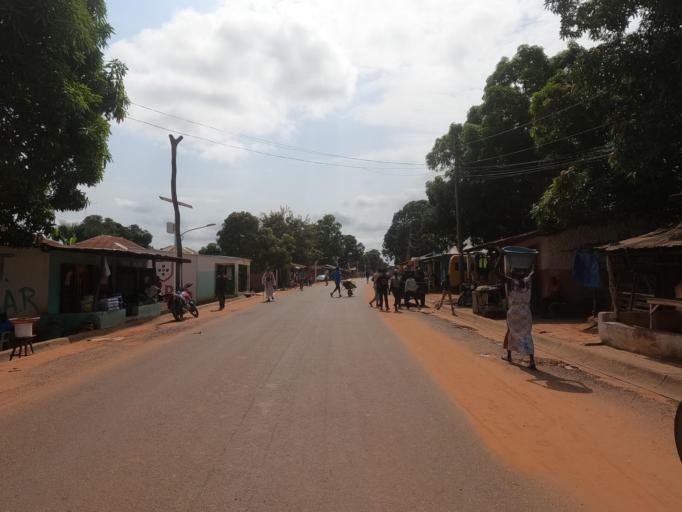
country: SN
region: Ziguinchor
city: Adeane
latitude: 12.4091
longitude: -15.7977
